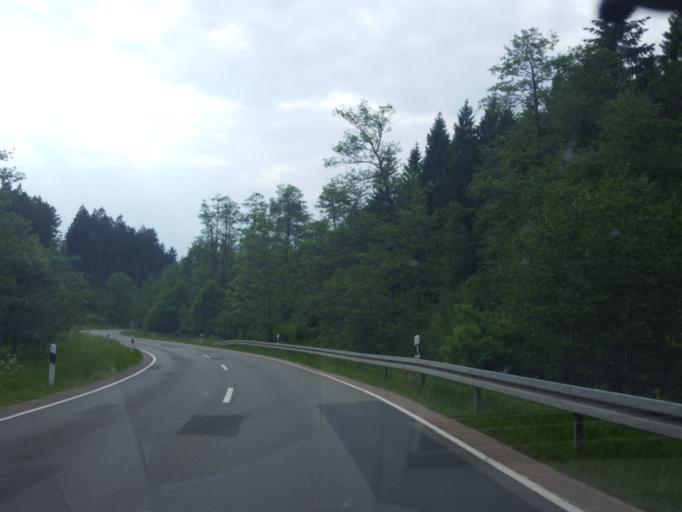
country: DE
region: Lower Saxony
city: Bad Grund
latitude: 51.8263
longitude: 10.2166
